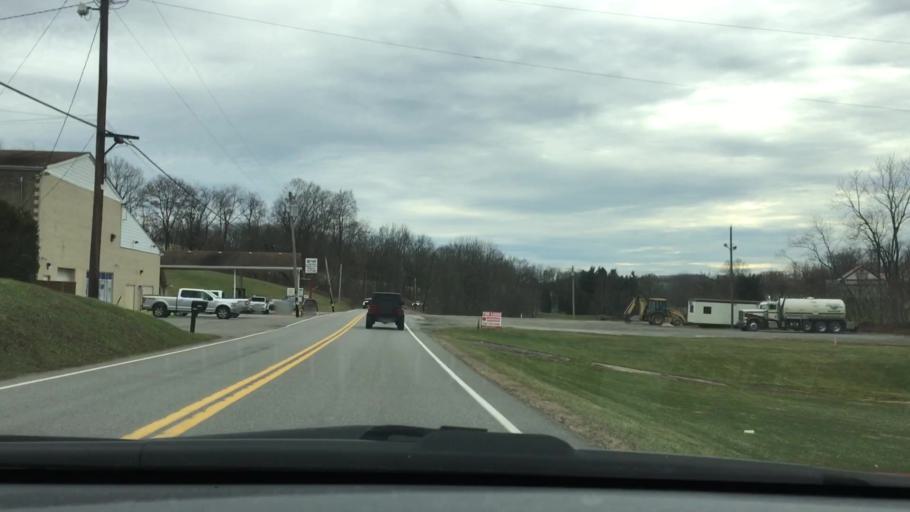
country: US
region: Pennsylvania
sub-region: Washington County
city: Muse
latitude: 40.2947
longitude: -80.2165
